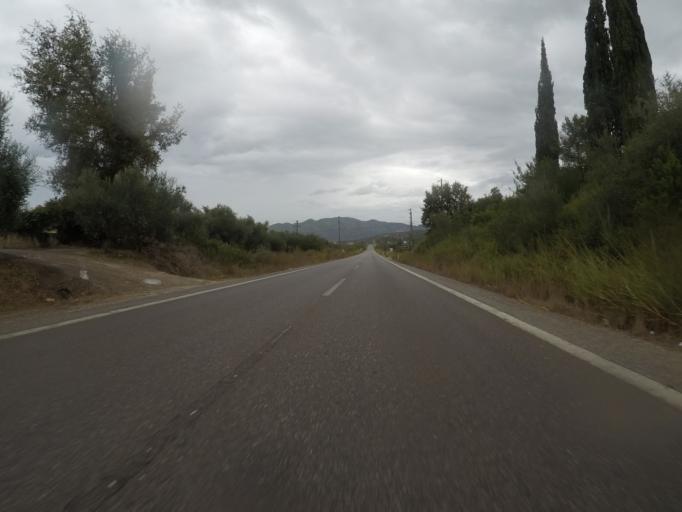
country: GR
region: West Greece
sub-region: Nomos Ileias
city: Zacharo
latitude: 37.4467
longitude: 21.6606
